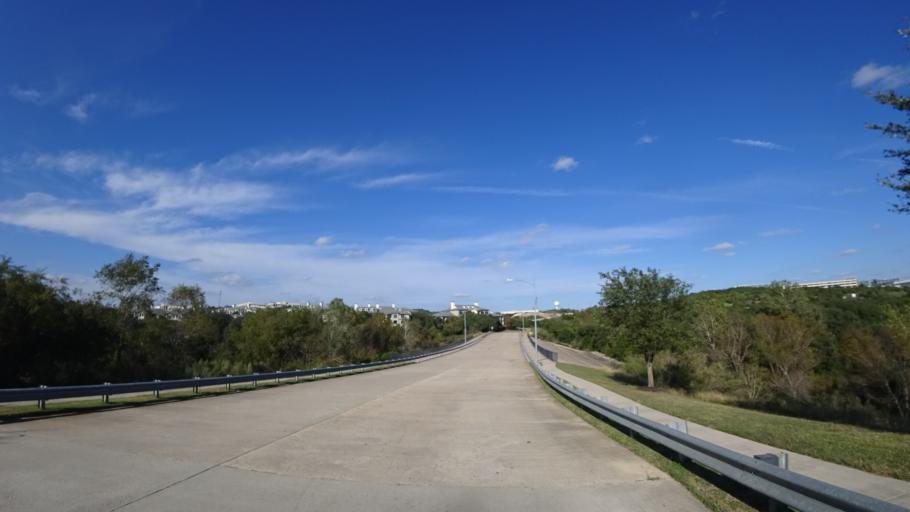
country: US
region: Texas
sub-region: Travis County
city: Barton Creek
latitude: 30.2491
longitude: -97.8701
